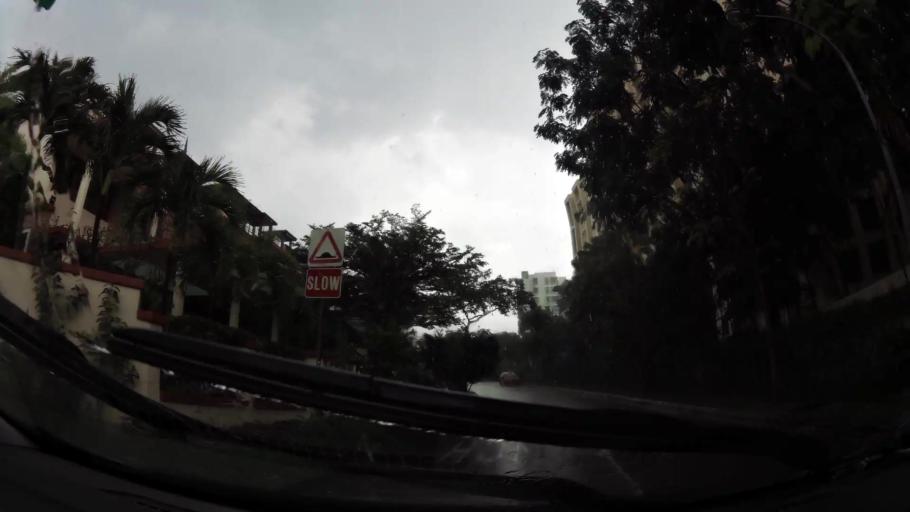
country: SG
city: Singapore
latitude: 1.3294
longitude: 103.9437
